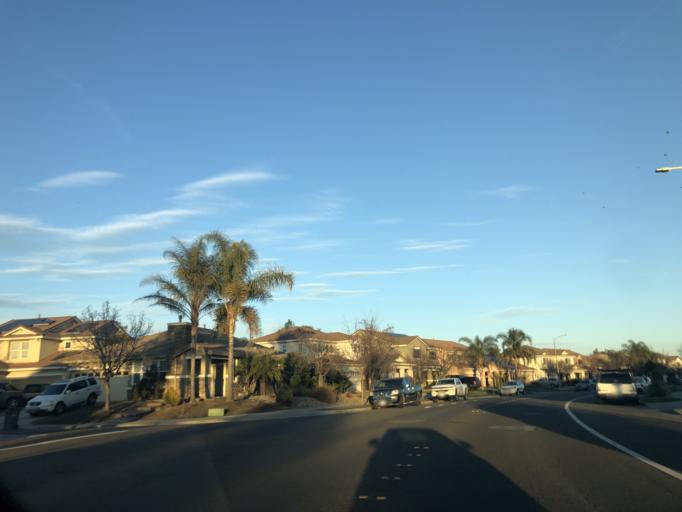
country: US
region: California
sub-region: Yolo County
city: Woodland
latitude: 38.6734
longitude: -121.7419
